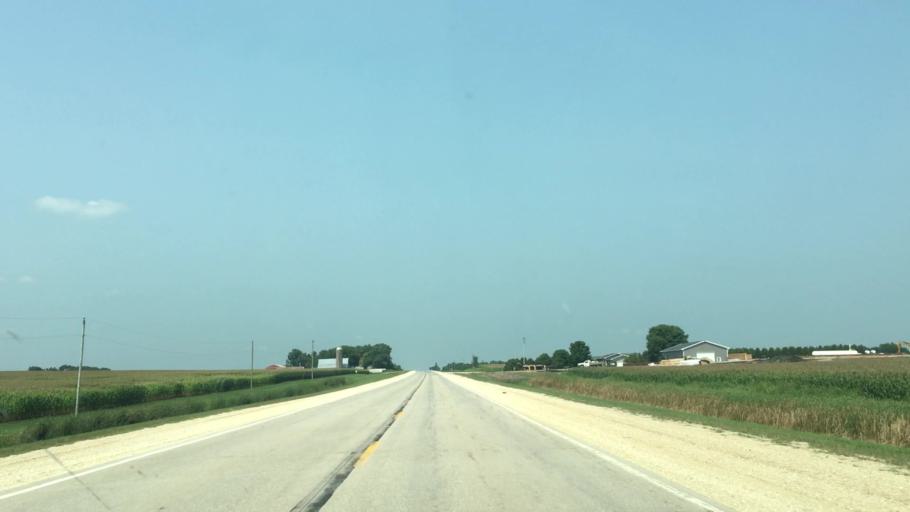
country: US
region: Iowa
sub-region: Fayette County
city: Fayette
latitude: 42.7645
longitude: -91.8045
